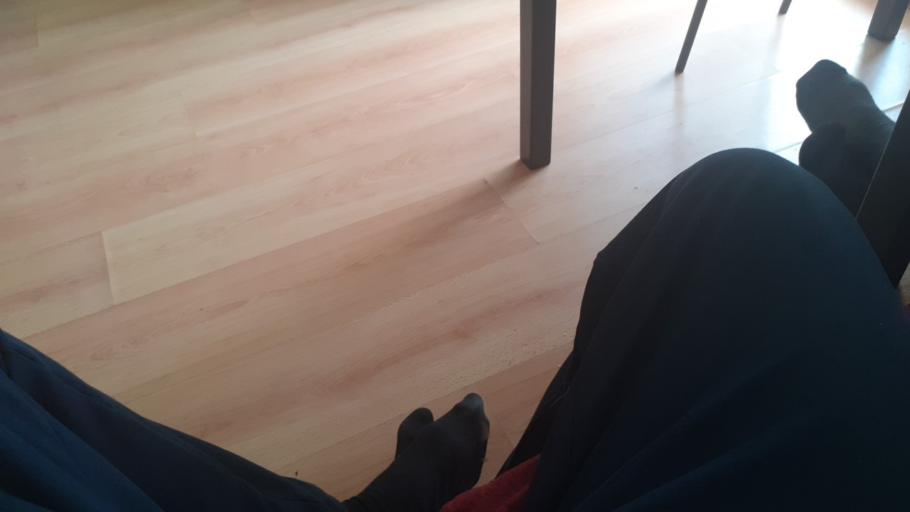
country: RU
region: Novosibirsk
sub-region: Novosibirskiy Rayon
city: Novosibirsk
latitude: 54.9937
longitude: 82.8870
